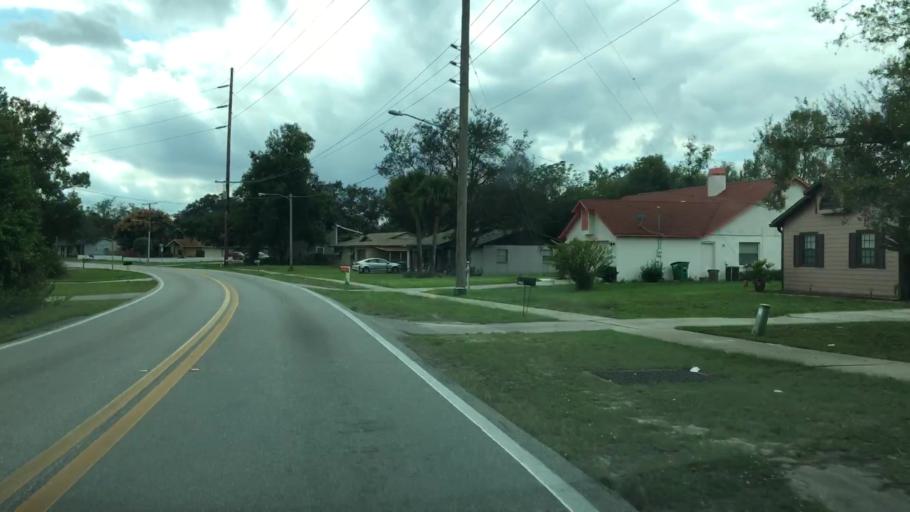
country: US
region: Florida
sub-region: Volusia County
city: Deltona
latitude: 28.8753
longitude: -81.2524
